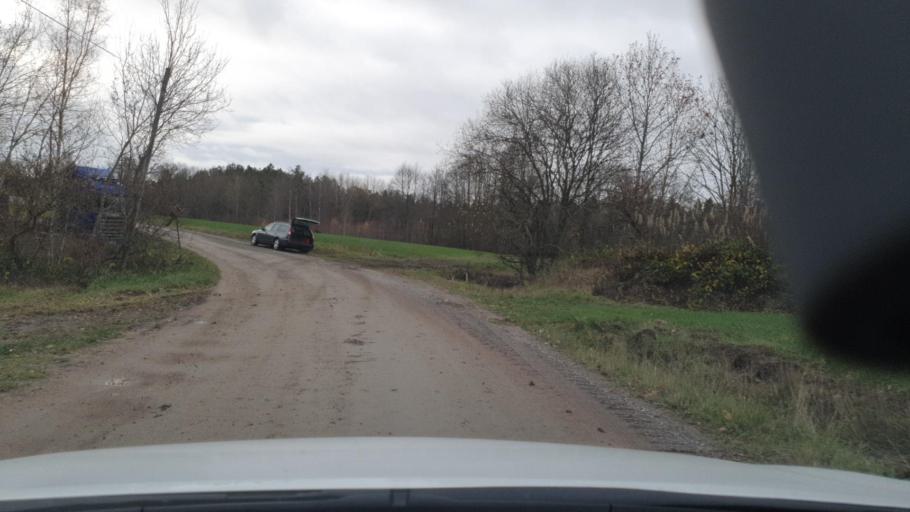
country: SE
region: Kalmar
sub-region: Vasterviks Kommun
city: Ankarsrum
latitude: 57.7057
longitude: 16.4525
